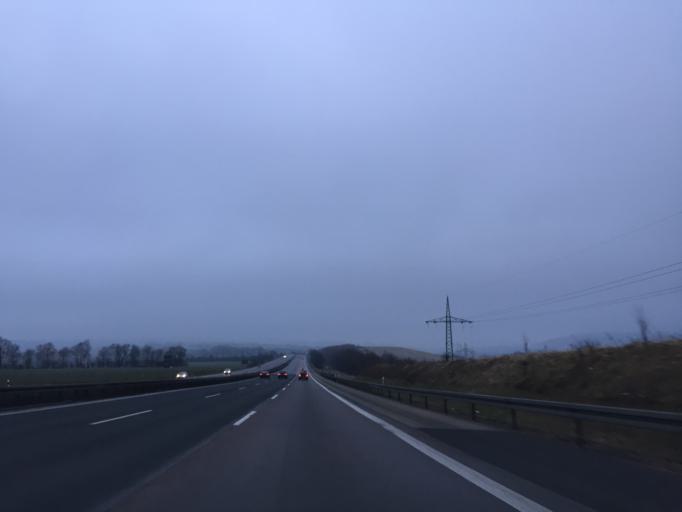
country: DE
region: Hesse
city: Bad Camberg
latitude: 50.2766
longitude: 8.2427
